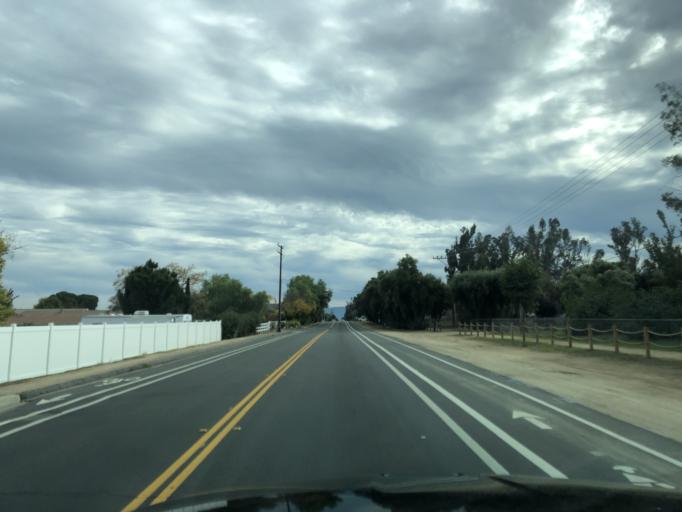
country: US
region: California
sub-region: Riverside County
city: Wildomar
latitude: 33.6034
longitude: -117.2872
